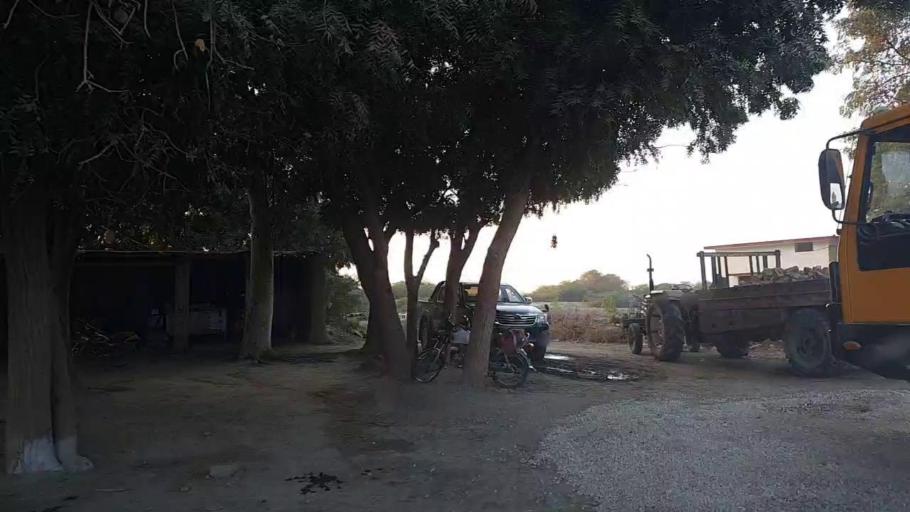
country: PK
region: Sindh
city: Naukot
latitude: 24.9498
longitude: 69.4299
